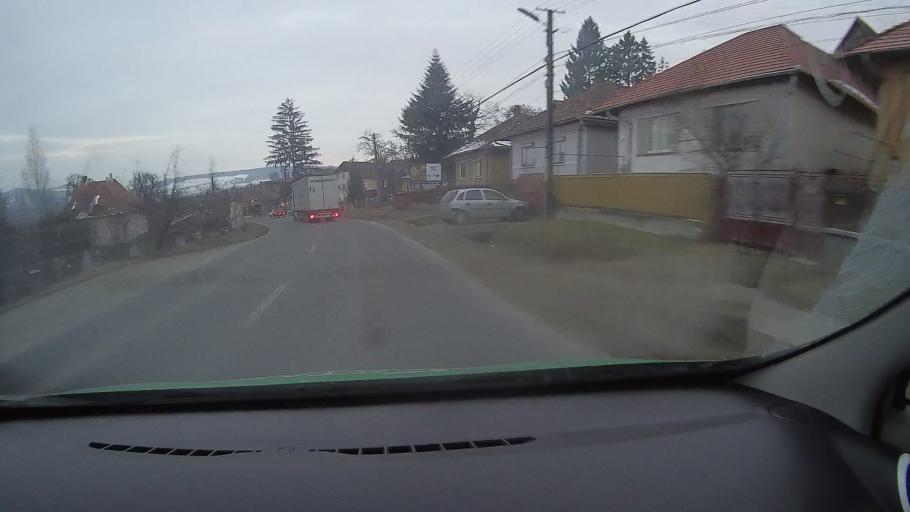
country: RO
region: Harghita
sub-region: Municipiul Odorheiu Secuiesc
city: Odorheiu Secuiesc
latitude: 46.3171
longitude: 25.2809
